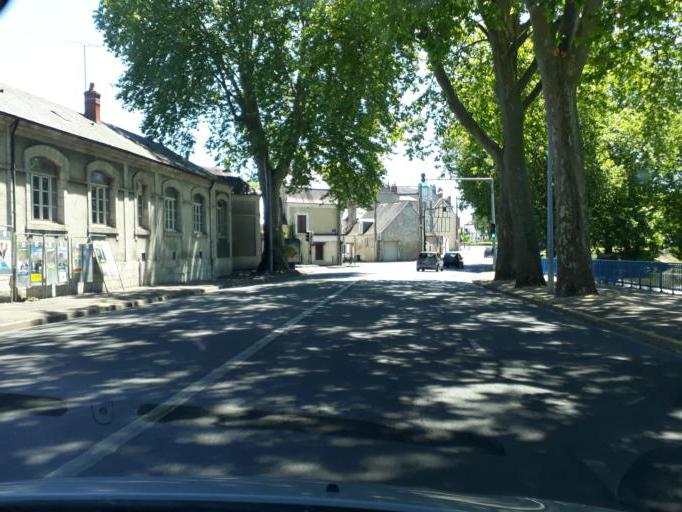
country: FR
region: Centre
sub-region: Departement du Cher
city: Bourges
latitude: 47.0816
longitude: 2.3893
